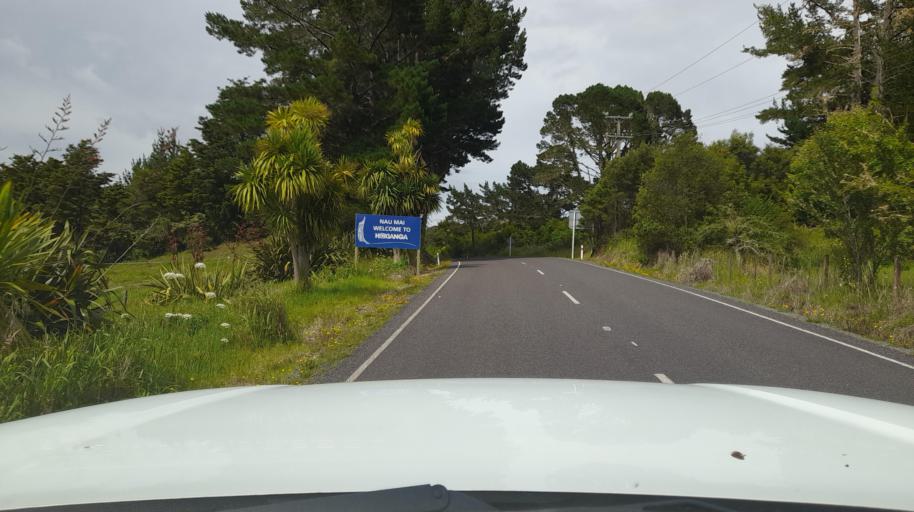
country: NZ
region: Northland
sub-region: Far North District
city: Taipa
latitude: -35.2376
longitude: 173.5429
